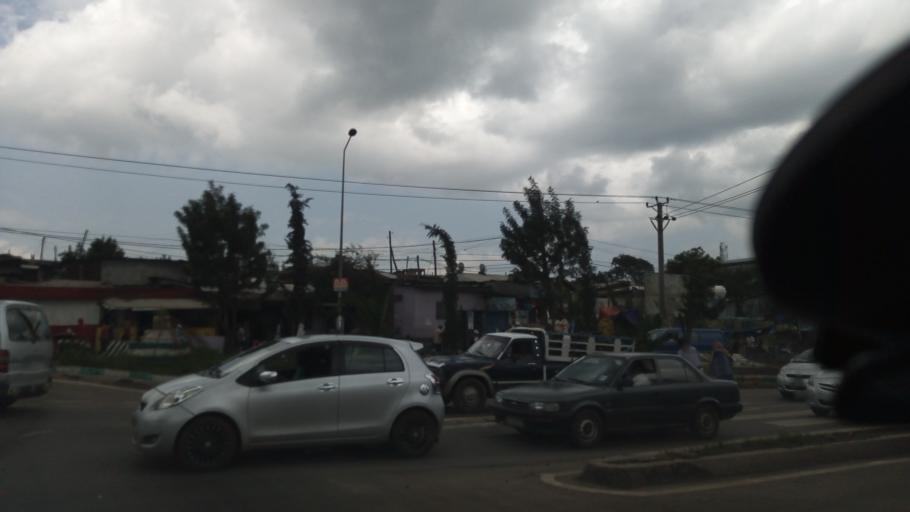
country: ET
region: Adis Abeba
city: Addis Ababa
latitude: 8.9928
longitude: 38.7169
